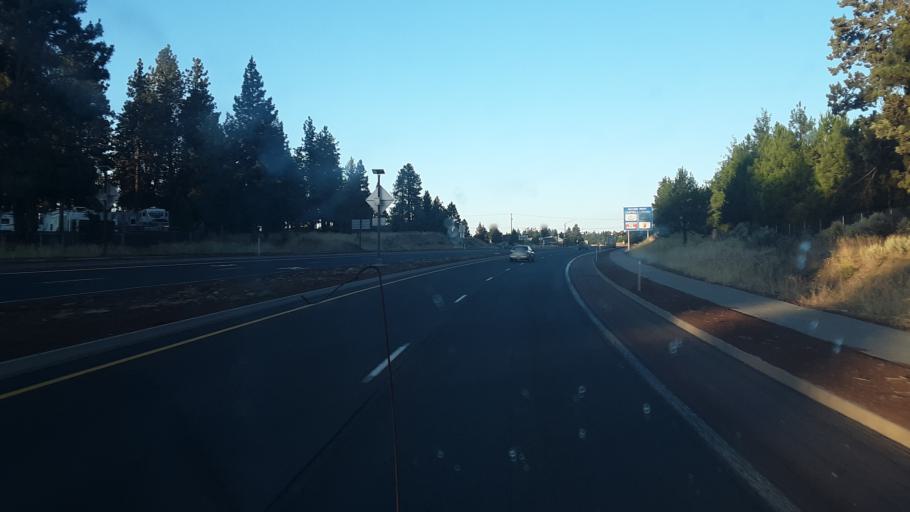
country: US
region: Oregon
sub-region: Deschutes County
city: Bend
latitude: 44.0314
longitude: -121.3147
